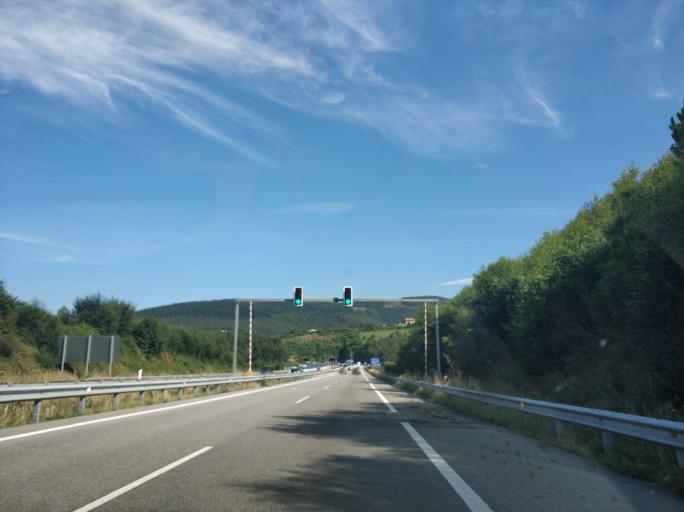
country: ES
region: Asturias
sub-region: Province of Asturias
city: Cudillero
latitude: 43.5474
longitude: -6.1614
